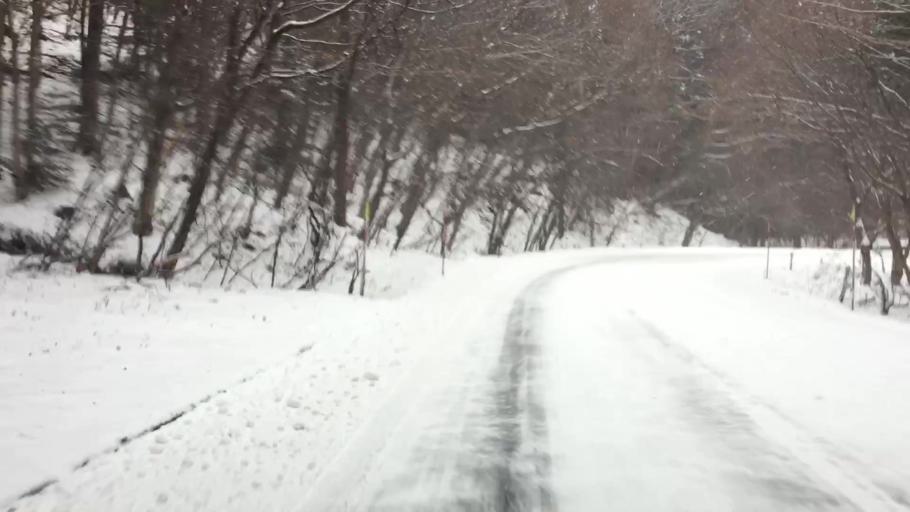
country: JP
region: Tochigi
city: Nikko
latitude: 36.8802
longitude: 139.7215
